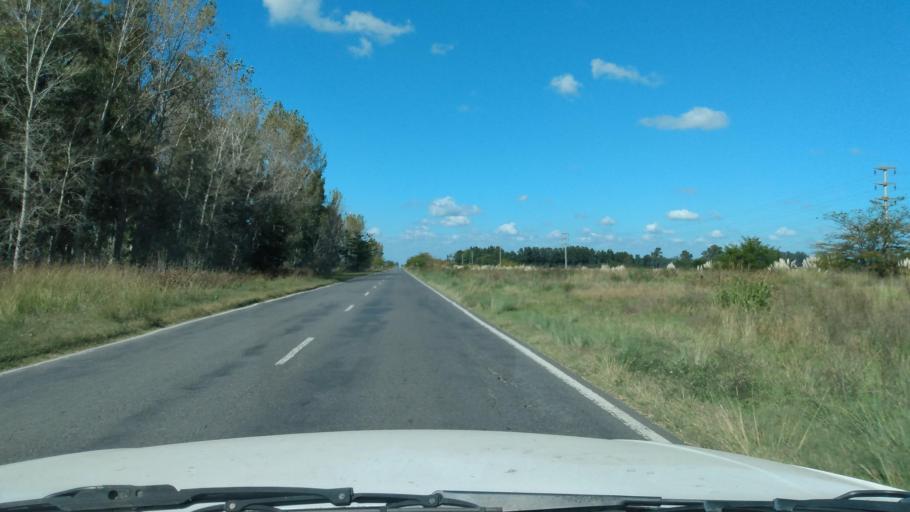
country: AR
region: Buenos Aires
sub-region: Partido de Mercedes
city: Mercedes
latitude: -34.7144
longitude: -59.3976
